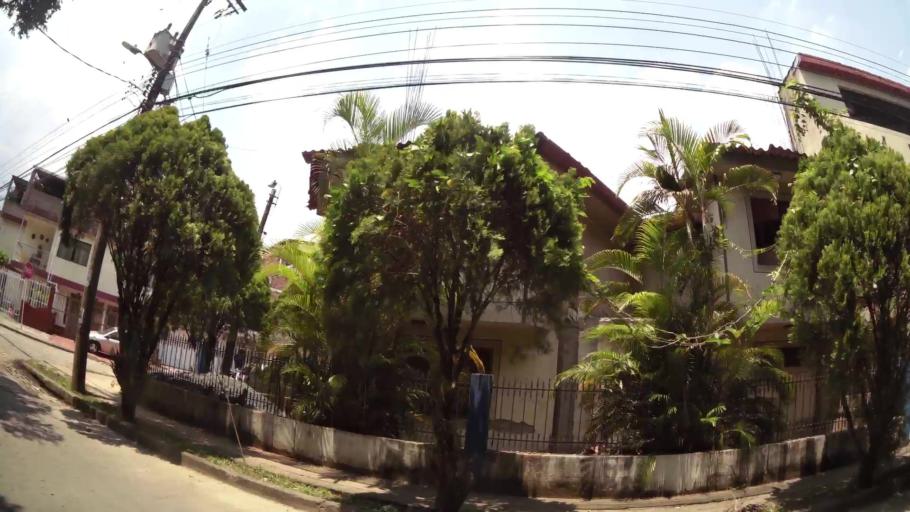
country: CO
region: Valle del Cauca
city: Cali
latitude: 3.4028
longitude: -76.5341
